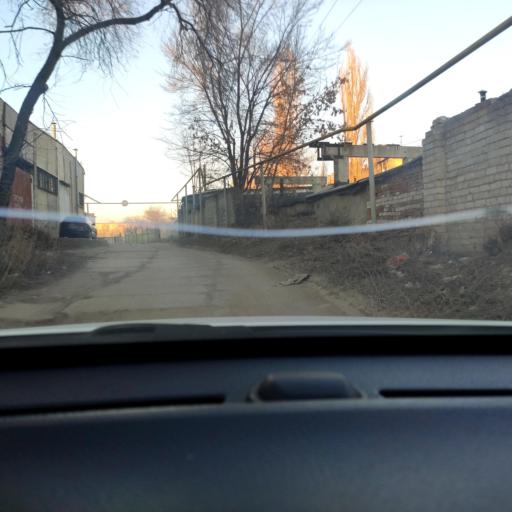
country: RU
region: Voronezj
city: Maslovka
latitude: 51.6123
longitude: 39.2426
